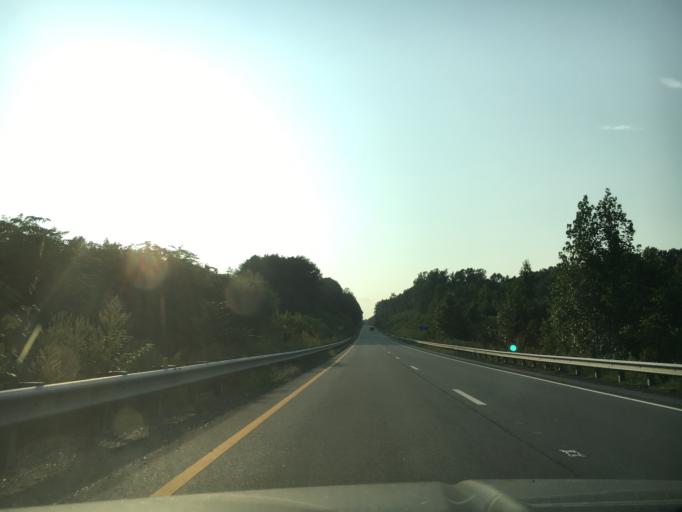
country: US
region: Virginia
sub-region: Appomattox County
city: Appomattox
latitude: 37.2709
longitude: -78.6699
